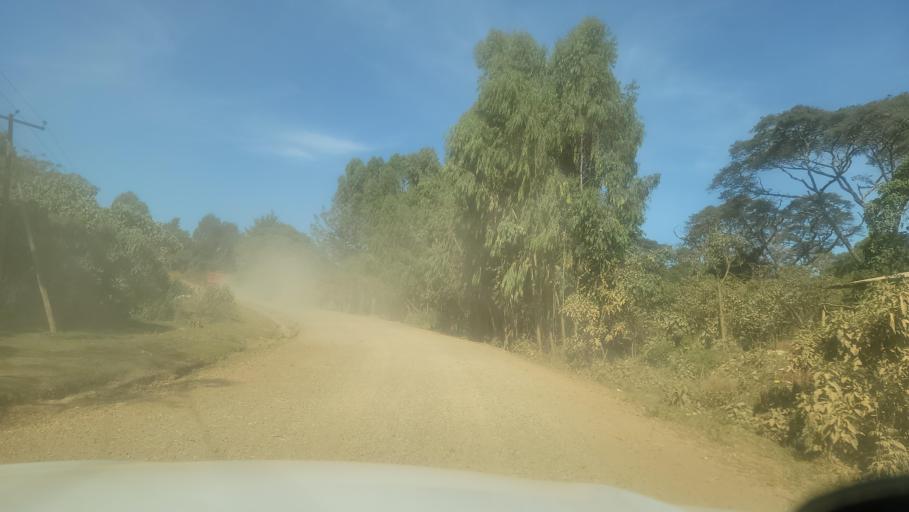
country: ET
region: Oromiya
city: Agaro
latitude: 7.8148
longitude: 36.5098
